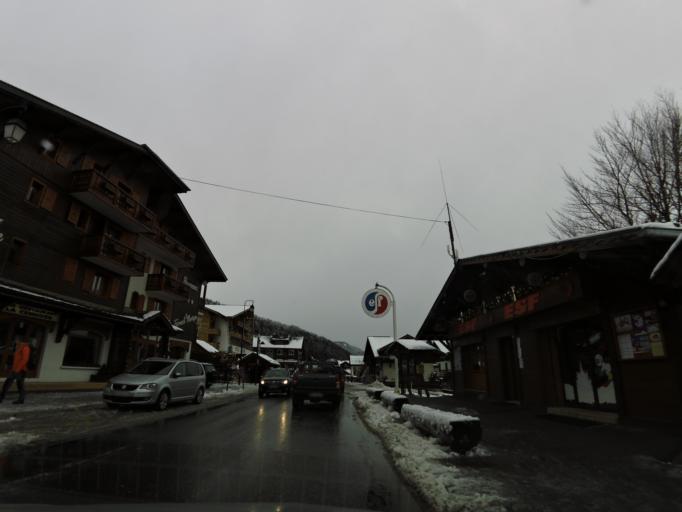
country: FR
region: Rhone-Alpes
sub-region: Departement de la Haute-Savoie
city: Morzine
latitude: 46.1797
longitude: 6.7035
